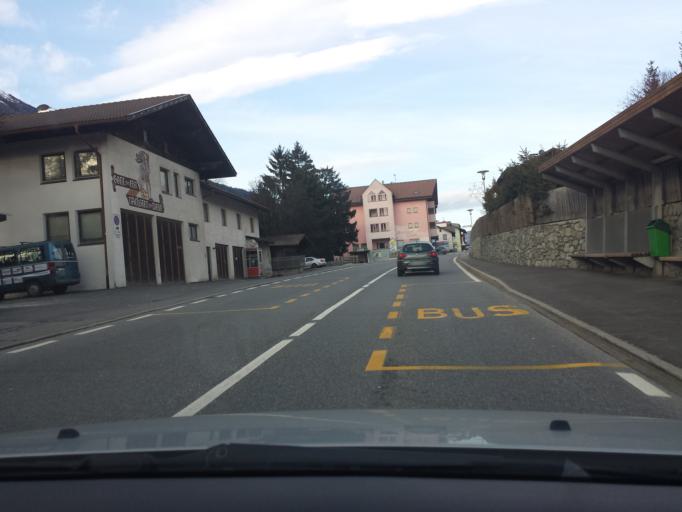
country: IT
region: Trentino-Alto Adige
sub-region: Bolzano
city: Curon Venosta
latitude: 46.7645
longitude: 10.5335
